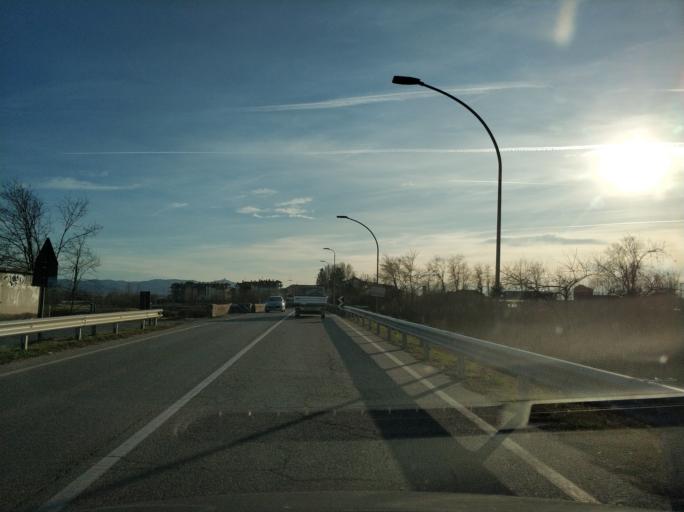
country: IT
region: Piedmont
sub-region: Provincia di Torino
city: Brandizzo
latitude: 45.1825
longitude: 7.8526
